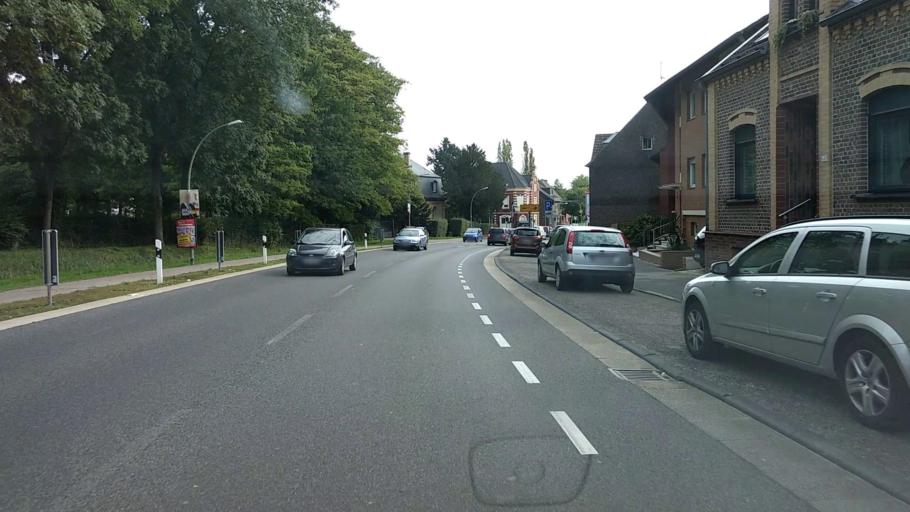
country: DE
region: North Rhine-Westphalia
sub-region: Regierungsbezirk Koln
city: Bergheim
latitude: 50.9425
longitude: 6.6780
